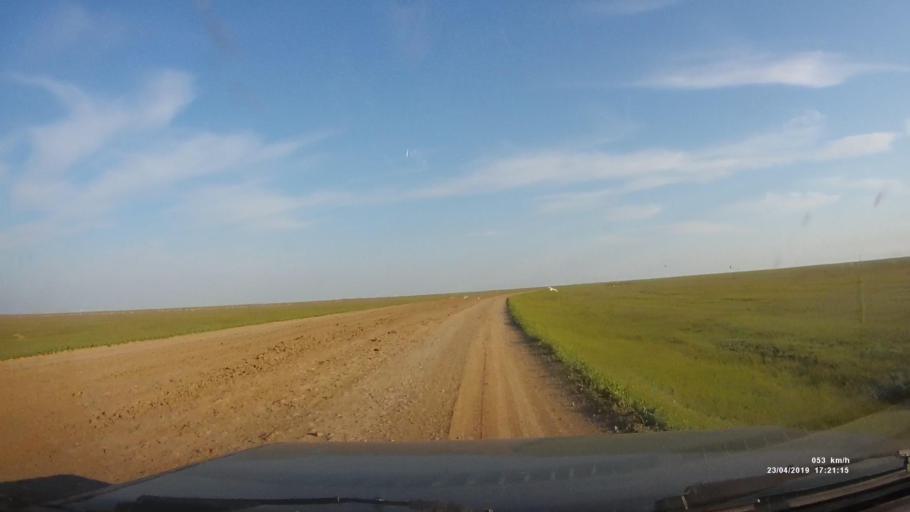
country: RU
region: Kalmykiya
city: Priyutnoye
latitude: 46.1775
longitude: 43.5046
